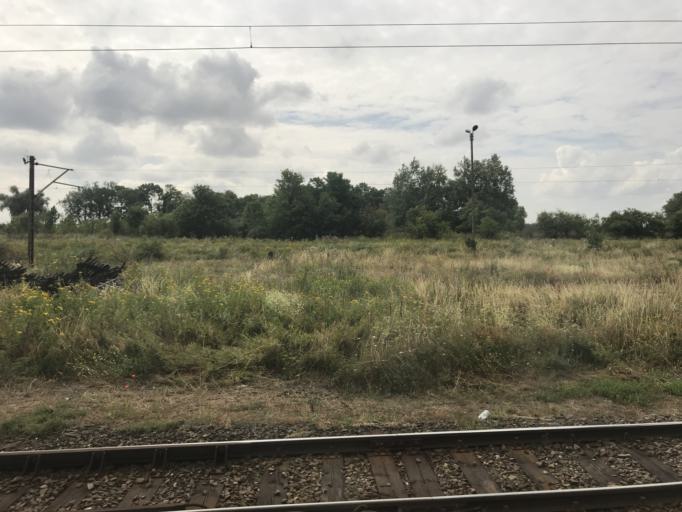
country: PL
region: Greater Poland Voivodeship
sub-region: Powiat gnieznienski
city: Gniezno
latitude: 52.5321
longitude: 17.6359
